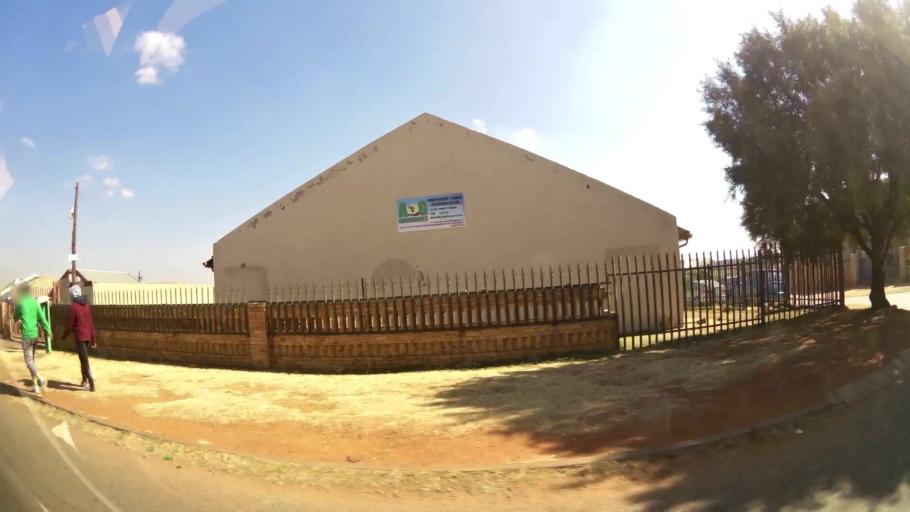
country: ZA
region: Gauteng
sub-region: West Rand District Municipality
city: Krugersdorp
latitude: -26.1506
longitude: 27.7715
